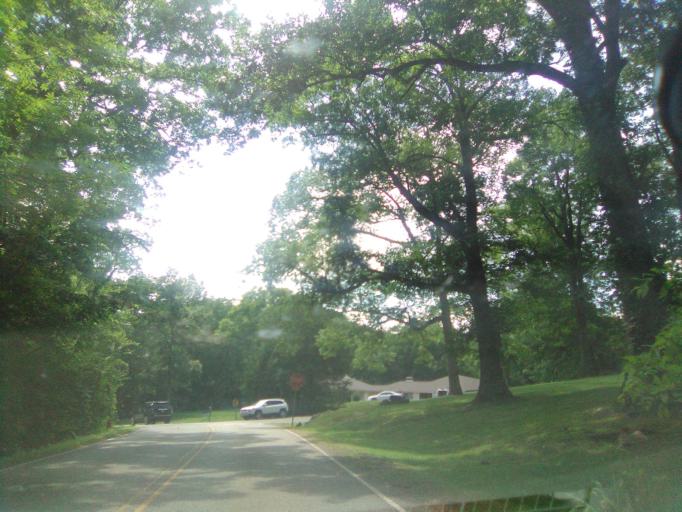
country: US
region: Tennessee
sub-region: Davidson County
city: Belle Meade
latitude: 36.1295
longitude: -86.8727
